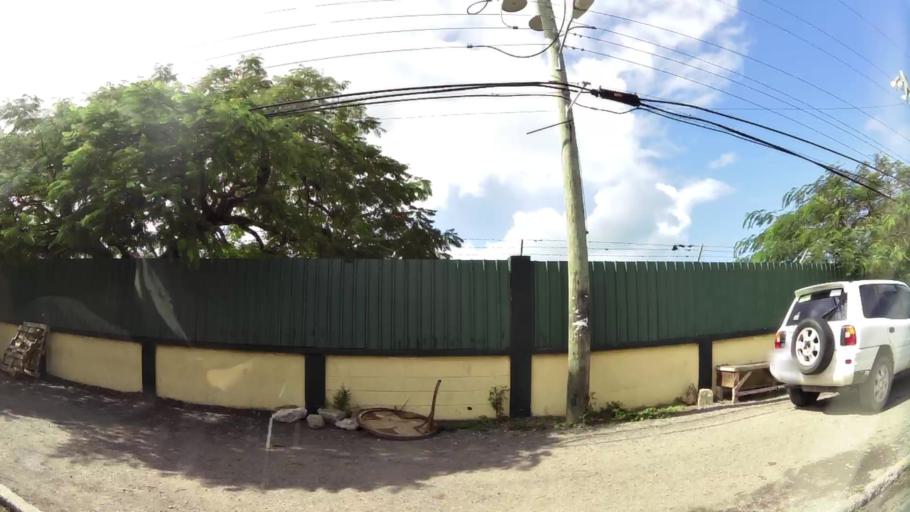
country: AG
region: Saint John
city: Saint John's
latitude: 17.1152
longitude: -61.8443
